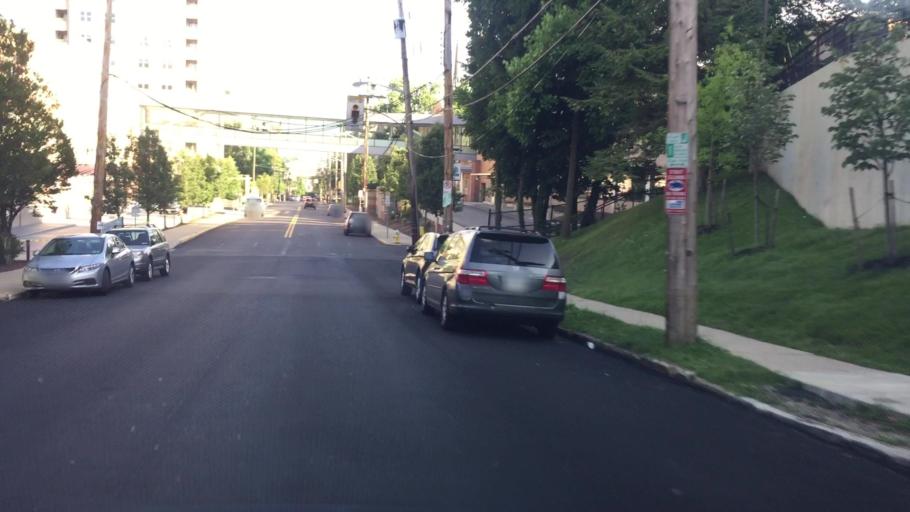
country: US
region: Pennsylvania
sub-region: Allegheny County
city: Bloomfield
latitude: 40.4505
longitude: -79.9537
